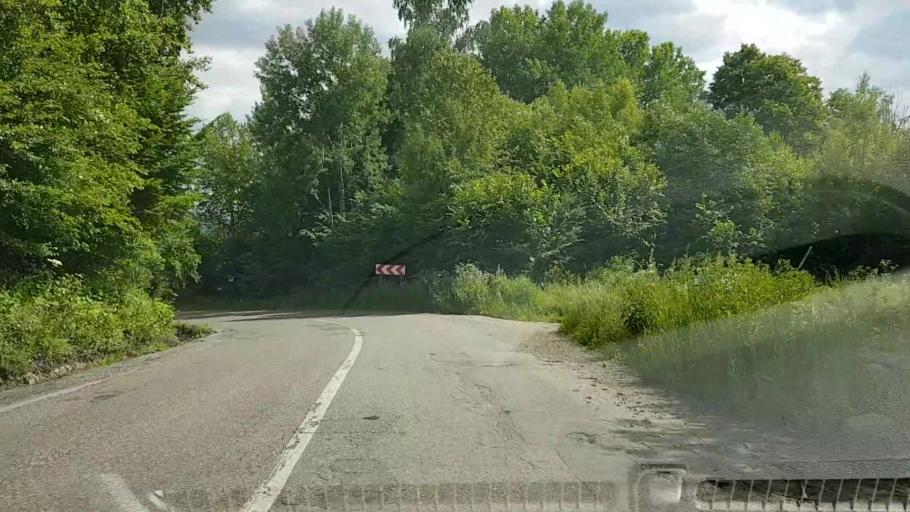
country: RO
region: Neamt
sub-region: Comuna Ceahlau
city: Ceahlau
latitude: 47.0637
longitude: 25.9628
